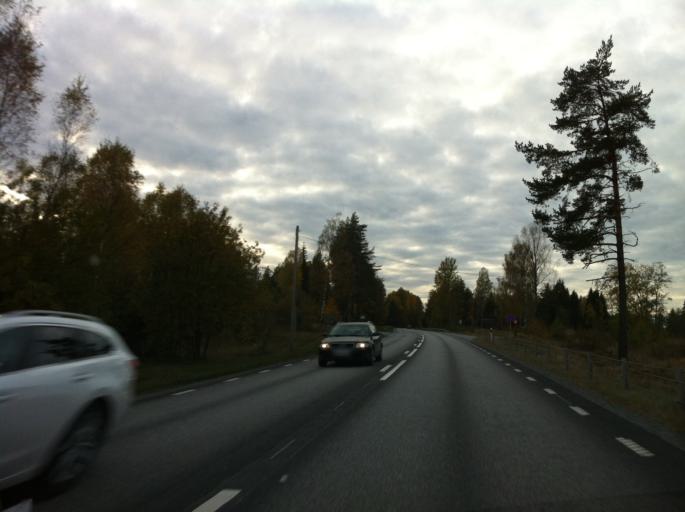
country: SE
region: OErebro
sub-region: Nora Kommun
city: Nora
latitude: 59.4647
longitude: 15.1315
